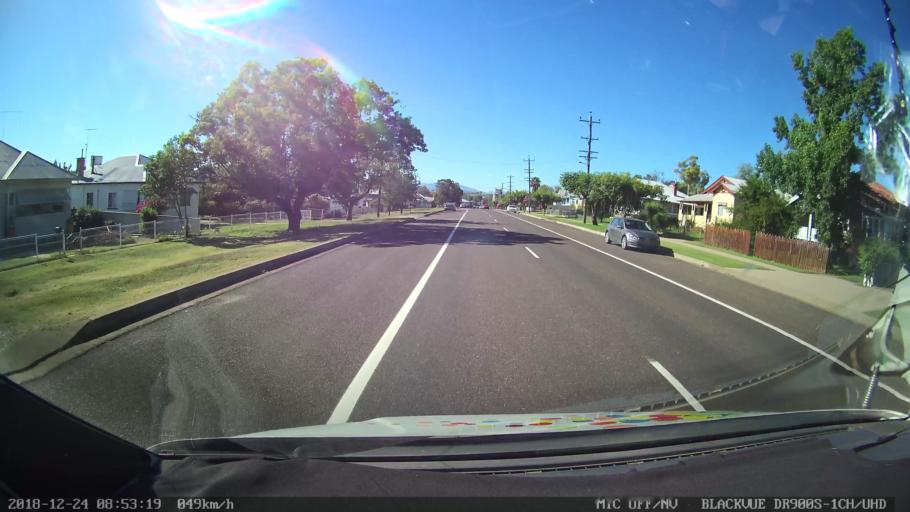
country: AU
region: New South Wales
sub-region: Liverpool Plains
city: Quirindi
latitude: -31.4974
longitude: 150.6812
